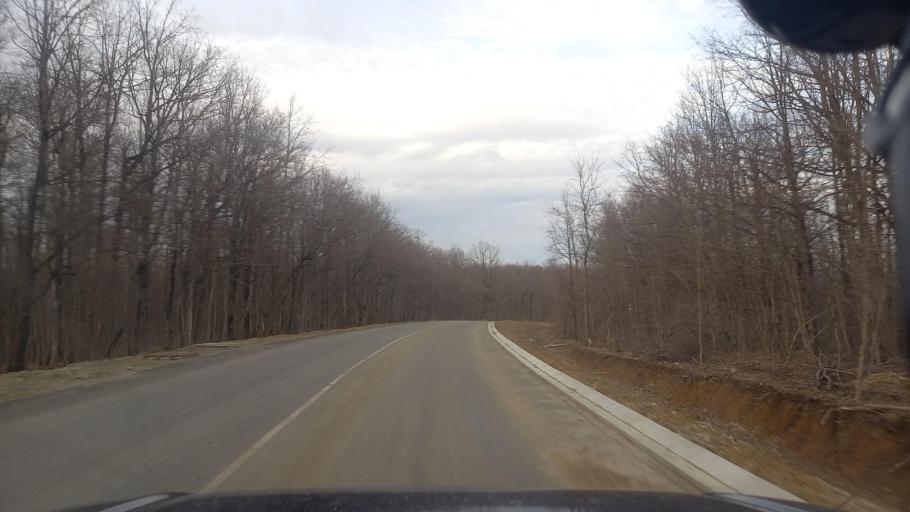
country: RU
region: Krasnodarskiy
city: Goryachiy Klyuch
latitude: 44.7071
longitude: 39.0048
